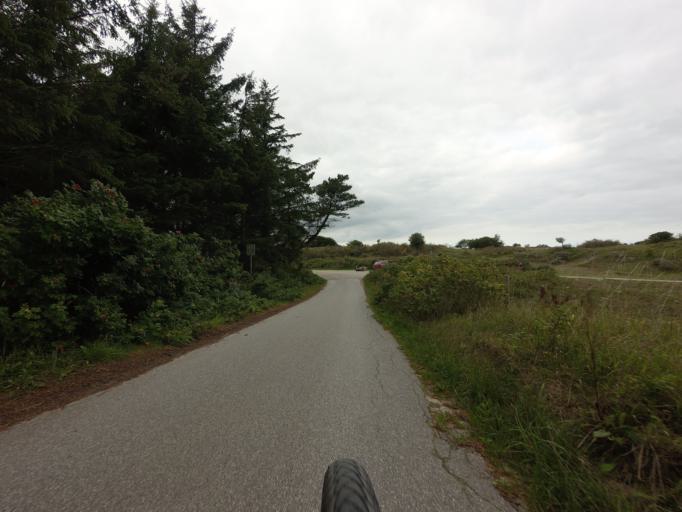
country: DK
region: North Denmark
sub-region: Hjorring Kommune
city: Sindal
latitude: 57.5864
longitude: 10.1428
